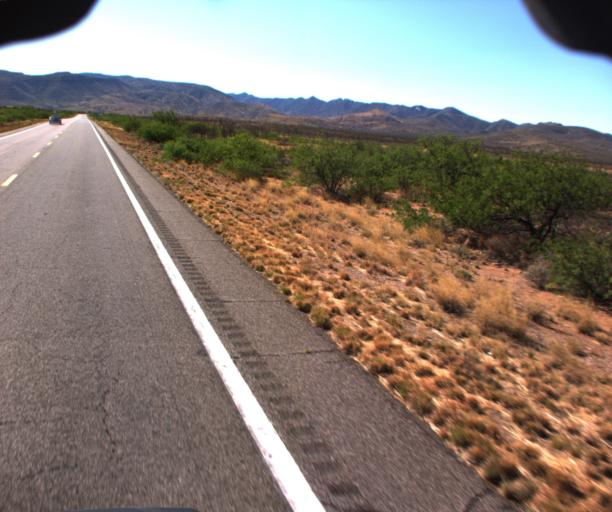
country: US
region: Arizona
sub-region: Cochise County
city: Bisbee
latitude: 31.5572
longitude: -110.0183
